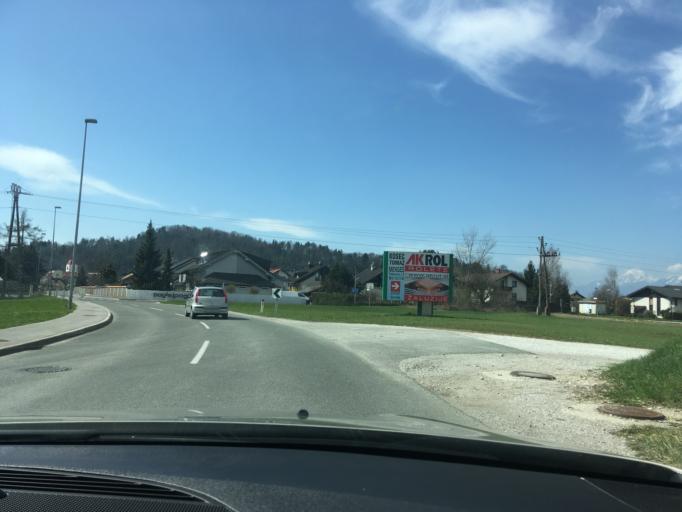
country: SI
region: Menges
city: Menges
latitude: 46.1627
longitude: 14.5774
